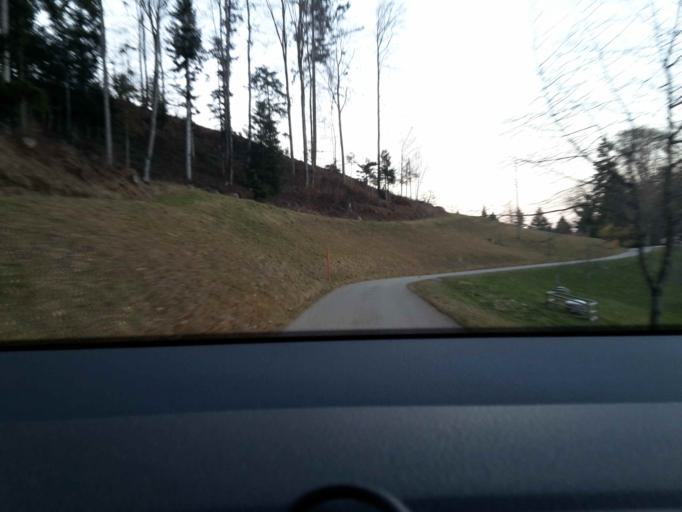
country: CH
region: Bern
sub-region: Oberaargau
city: Rohrbach
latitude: 47.1250
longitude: 7.7951
